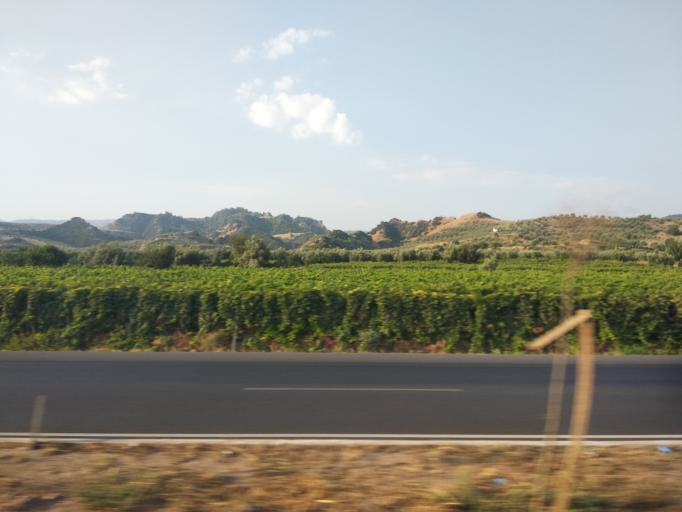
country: TR
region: Manisa
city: Ahmetli
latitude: 38.5076
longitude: 27.9900
